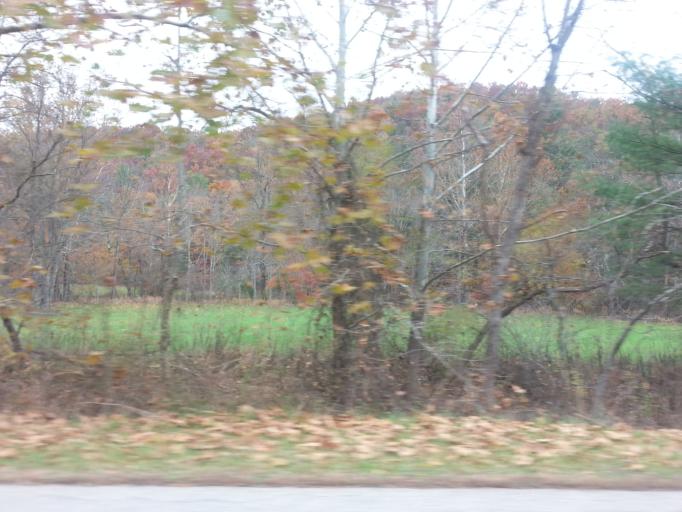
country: US
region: Virginia
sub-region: Pulaski County
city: Pulaski
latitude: 37.0896
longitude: -80.9176
